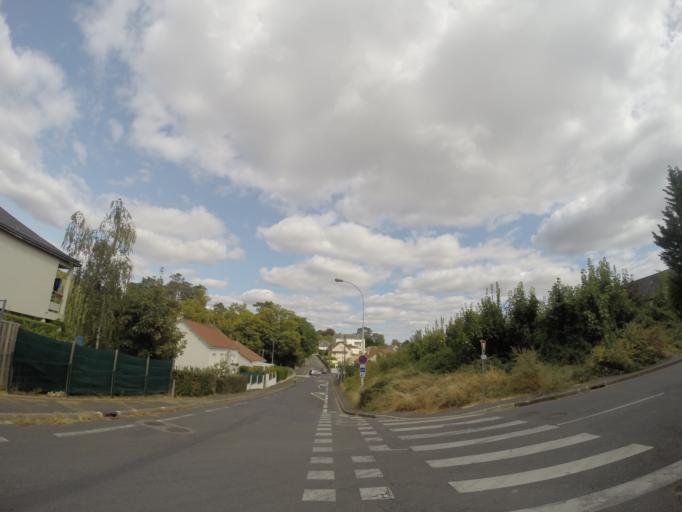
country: FR
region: Centre
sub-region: Departement d'Indre-et-Loire
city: Tours
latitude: 47.4094
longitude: 0.7064
